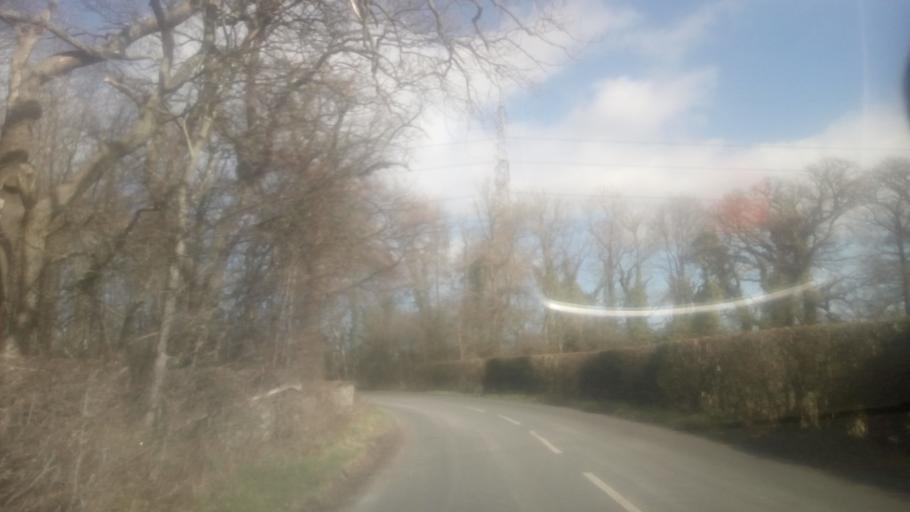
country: GB
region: Scotland
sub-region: East Lothian
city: Ormiston
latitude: 55.8921
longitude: -2.9535
